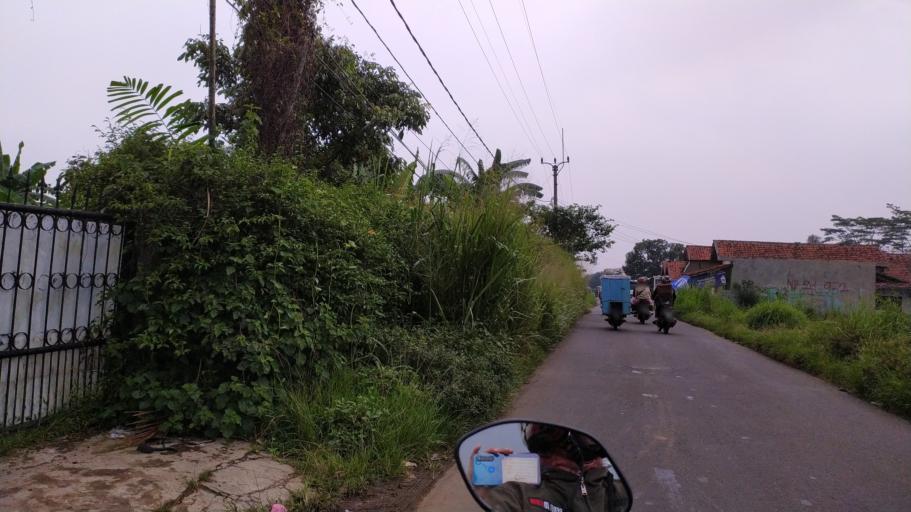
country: ID
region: West Java
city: Ciampea
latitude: -6.6004
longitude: 106.7031
